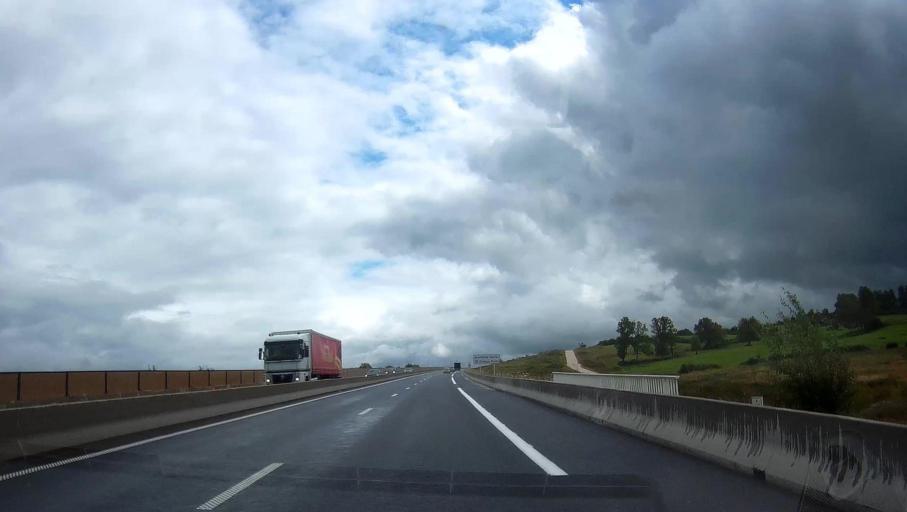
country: FR
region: Champagne-Ardenne
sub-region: Departement des Ardennes
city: Tournes
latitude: 49.7844
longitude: 4.5978
